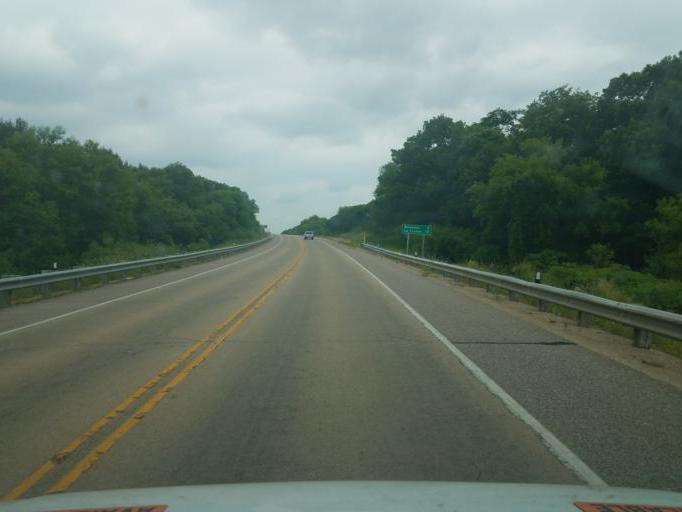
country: US
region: Wisconsin
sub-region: Sauk County
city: Reedsburg
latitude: 43.5964
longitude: -90.1280
